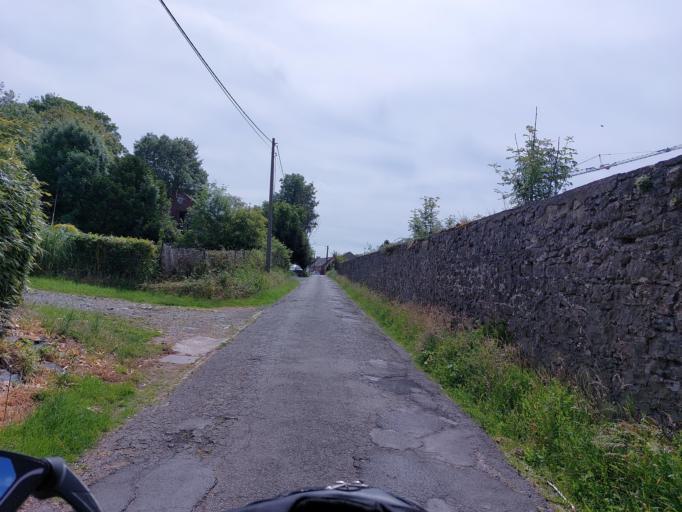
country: BE
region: Wallonia
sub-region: Province du Hainaut
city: Chievres
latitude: 50.5894
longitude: 3.8071
